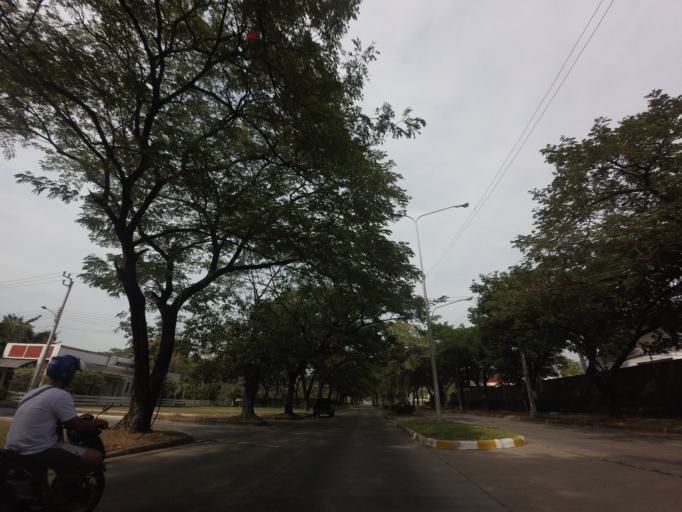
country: TH
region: Bangkok
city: Khlong Sam Wa
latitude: 13.8740
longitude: 100.7085
